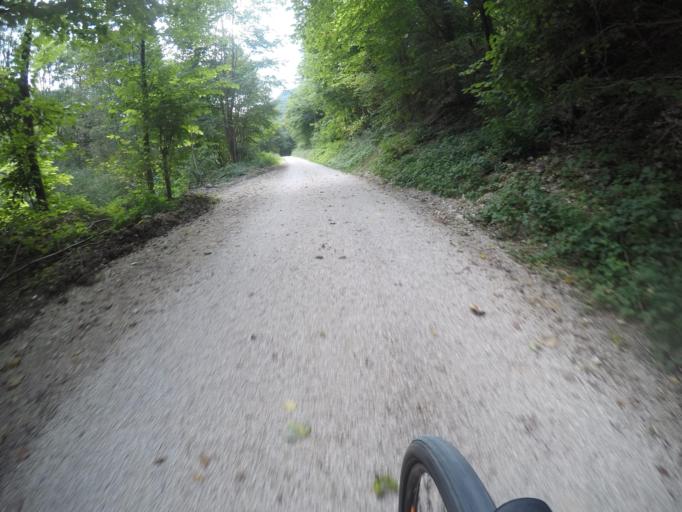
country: DE
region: Baden-Wuerttemberg
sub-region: Tuebingen Region
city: Bad Urach
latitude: 48.4810
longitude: 9.4020
